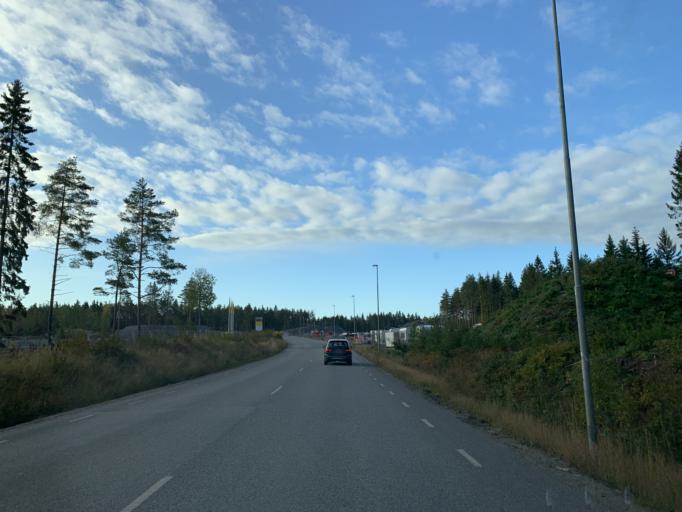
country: SE
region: Stockholm
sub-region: Upplands-Bro Kommun
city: Bro
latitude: 59.5078
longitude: 17.6150
